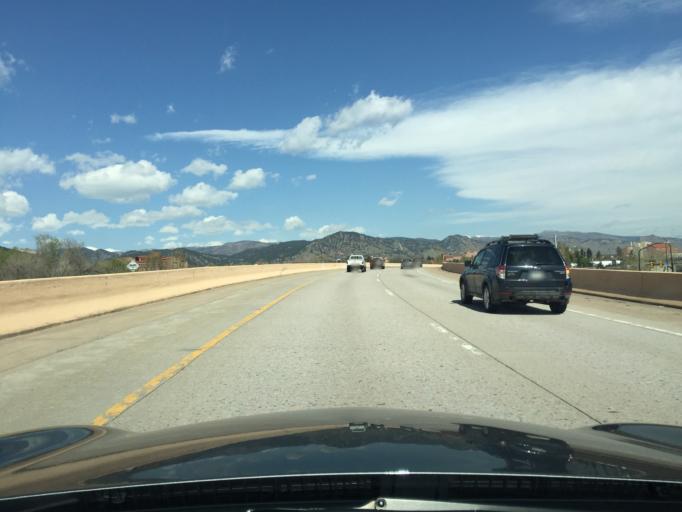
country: US
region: Colorado
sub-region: Boulder County
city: Boulder
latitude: 39.9992
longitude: -105.2567
